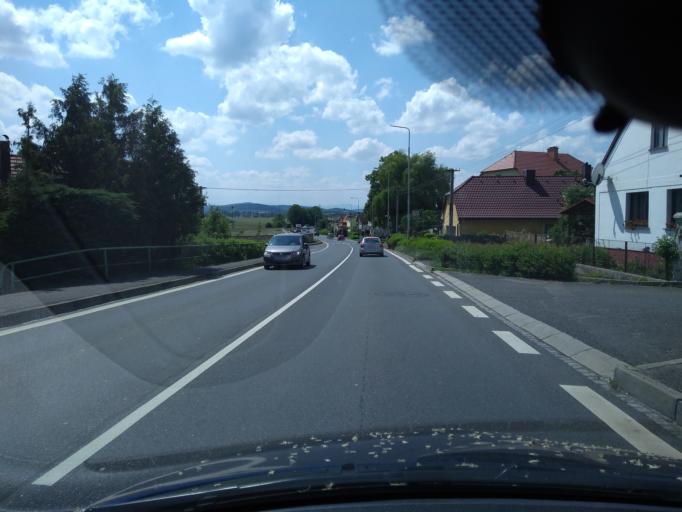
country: CZ
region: Plzensky
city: Svihov
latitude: 49.5016
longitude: 13.2938
